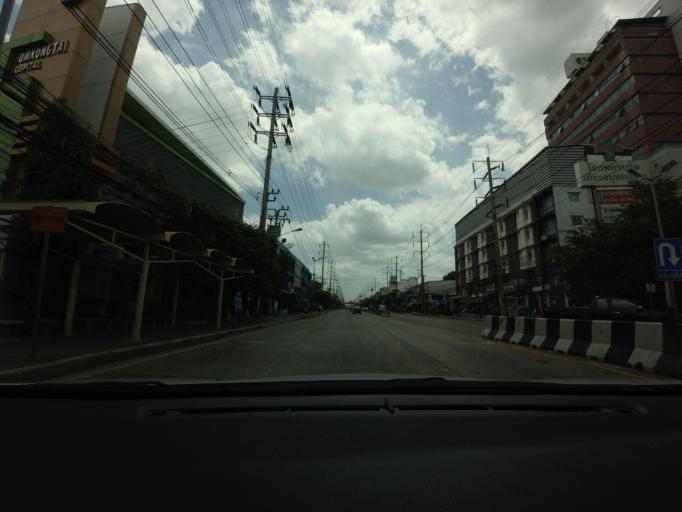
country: TH
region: Samut Prakan
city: Phra Samut Chedi
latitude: 13.6460
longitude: 100.5786
